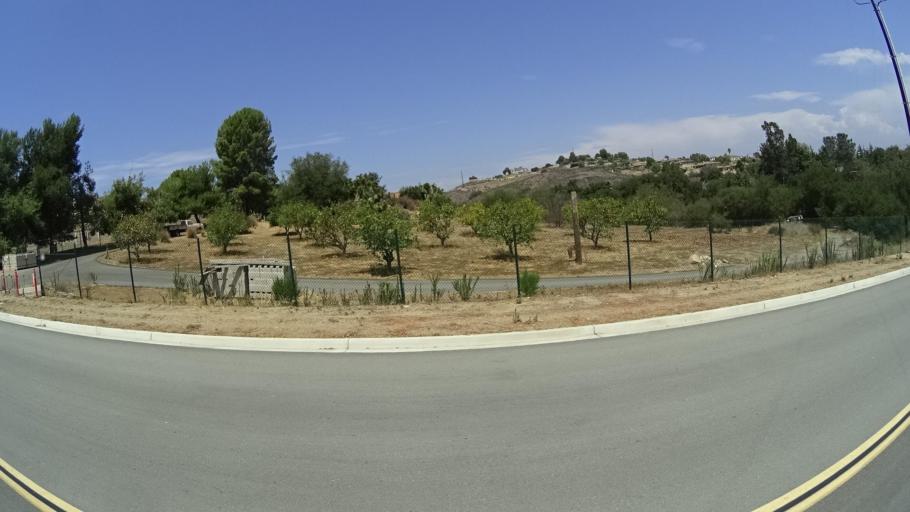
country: US
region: California
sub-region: San Diego County
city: Bonsall
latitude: 33.3238
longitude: -117.2082
